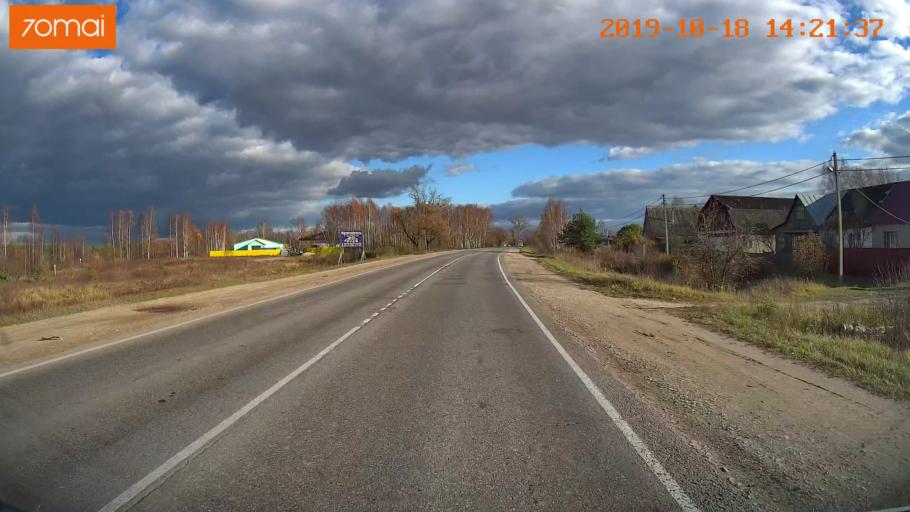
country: RU
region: Rjazan
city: Tuma
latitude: 55.1468
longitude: 40.4609
